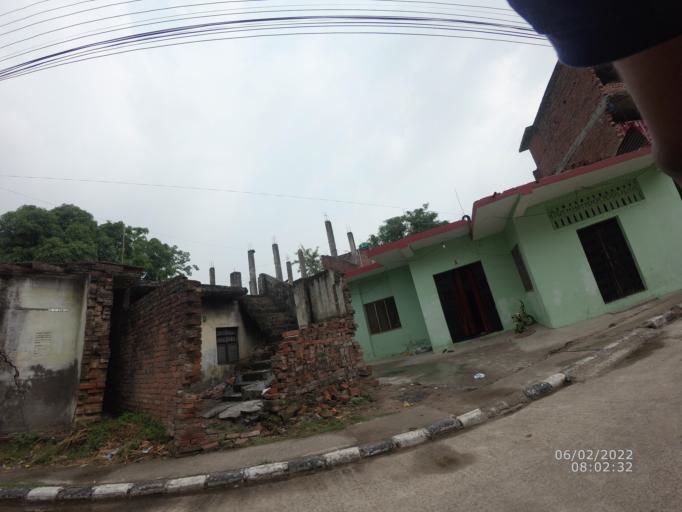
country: NP
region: Western Region
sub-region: Lumbini Zone
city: Bhairahawa
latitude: 27.4795
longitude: 83.4746
